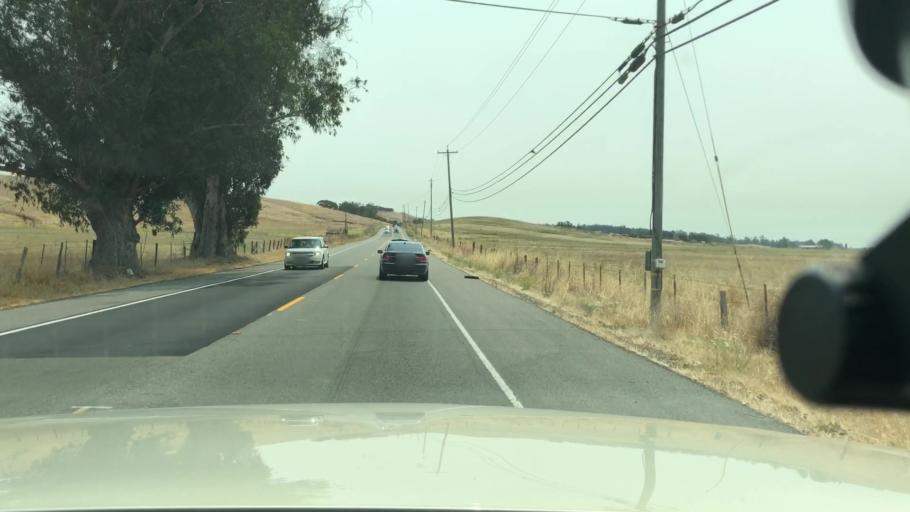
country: US
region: California
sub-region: Sonoma County
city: Petaluma
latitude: 38.2210
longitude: -122.5654
